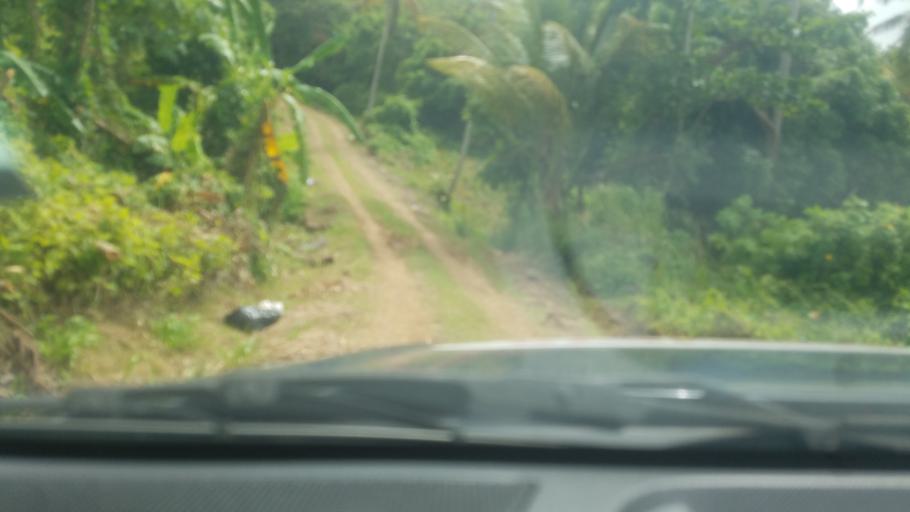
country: LC
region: Micoud Quarter
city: Micoud
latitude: 13.8030
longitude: -60.9315
